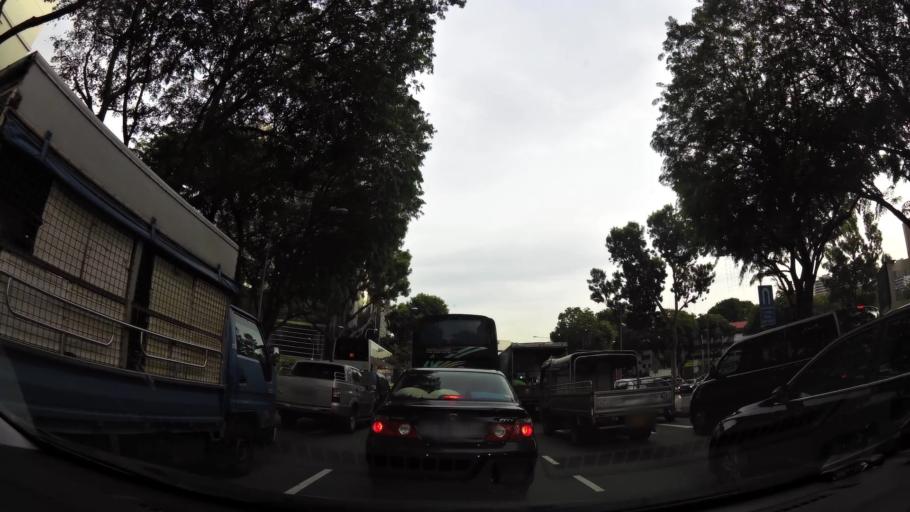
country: SG
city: Singapore
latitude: 1.2880
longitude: 103.8040
